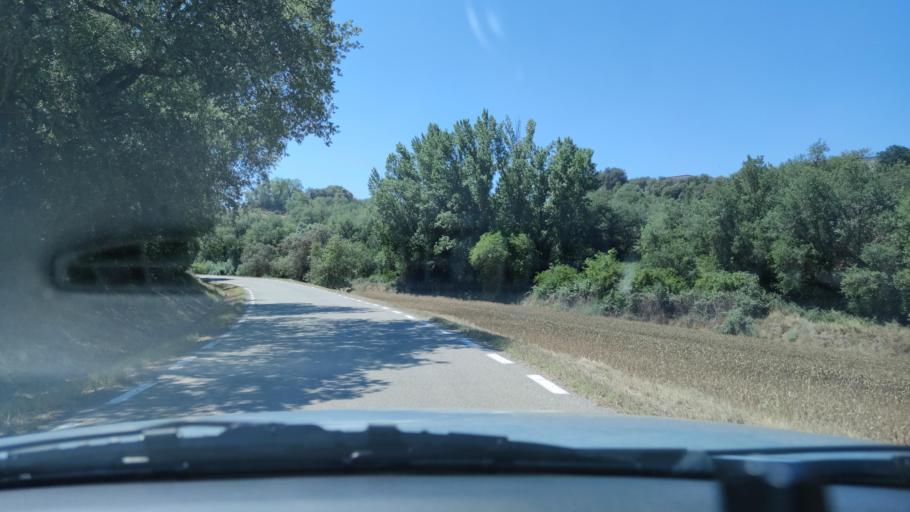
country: ES
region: Catalonia
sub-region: Provincia de Lleida
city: Tora de Riubregos
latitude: 41.8386
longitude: 1.4217
